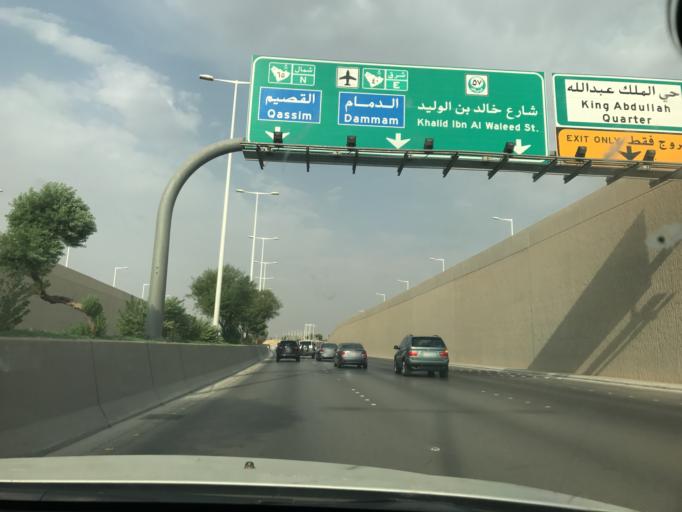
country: SA
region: Ar Riyad
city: Riyadh
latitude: 24.7339
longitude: 46.7377
